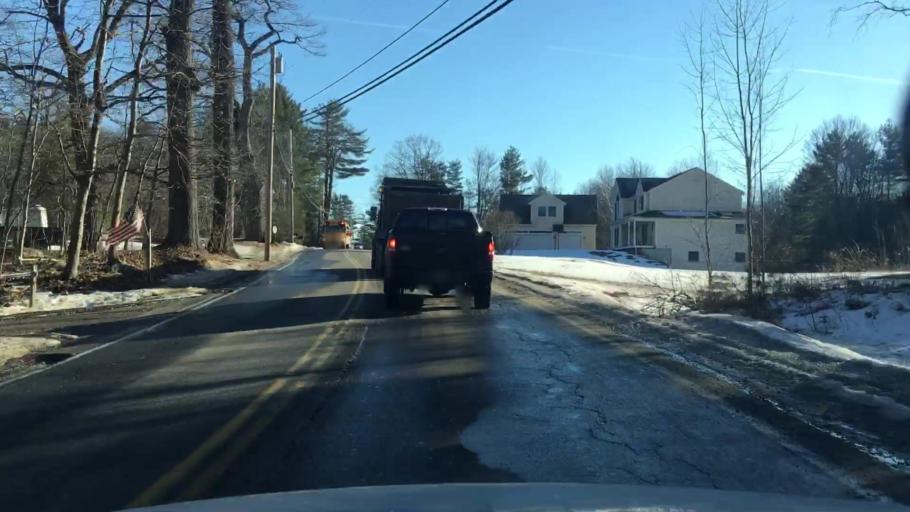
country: US
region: Maine
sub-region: Cumberland County
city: Westbrook
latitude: 43.7139
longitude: -70.3598
